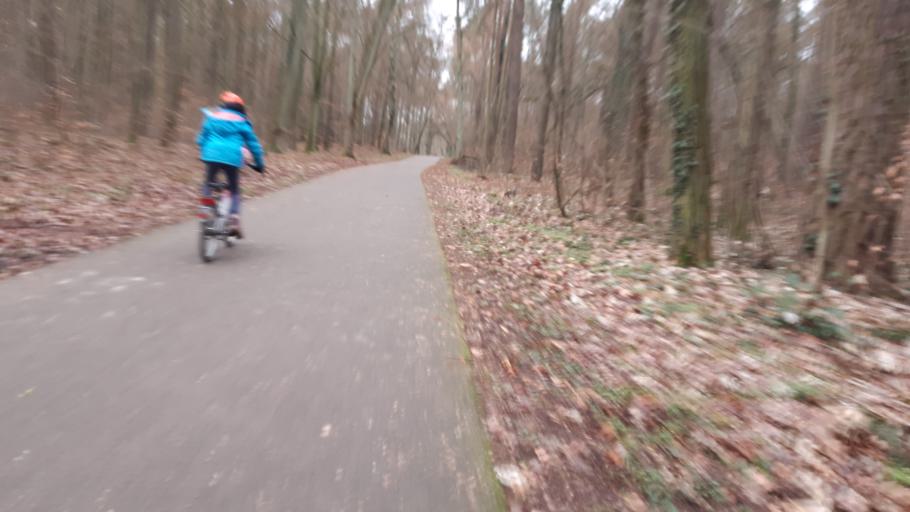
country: DE
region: Brandenburg
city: Templin
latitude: 53.1151
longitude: 13.5250
